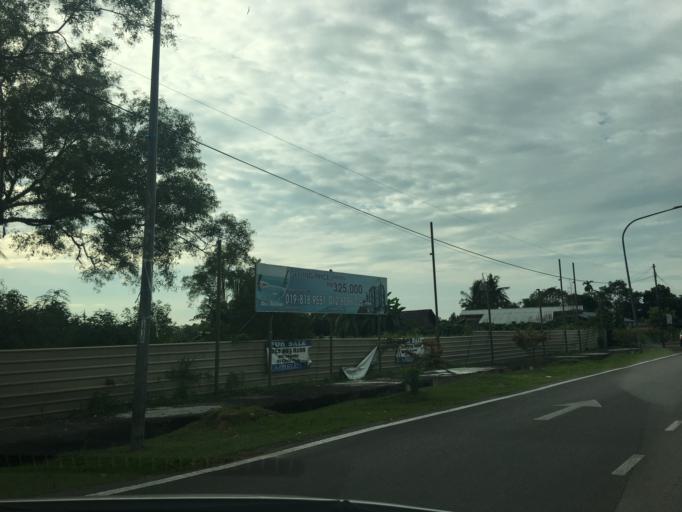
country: MY
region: Sarawak
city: Kuching
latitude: 1.5591
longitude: 110.3288
